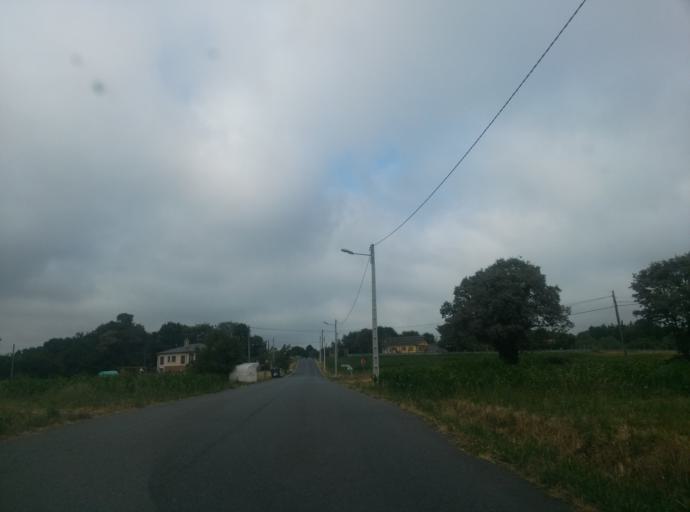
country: ES
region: Galicia
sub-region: Provincia de Lugo
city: Lugo
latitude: 43.0624
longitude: -7.5647
